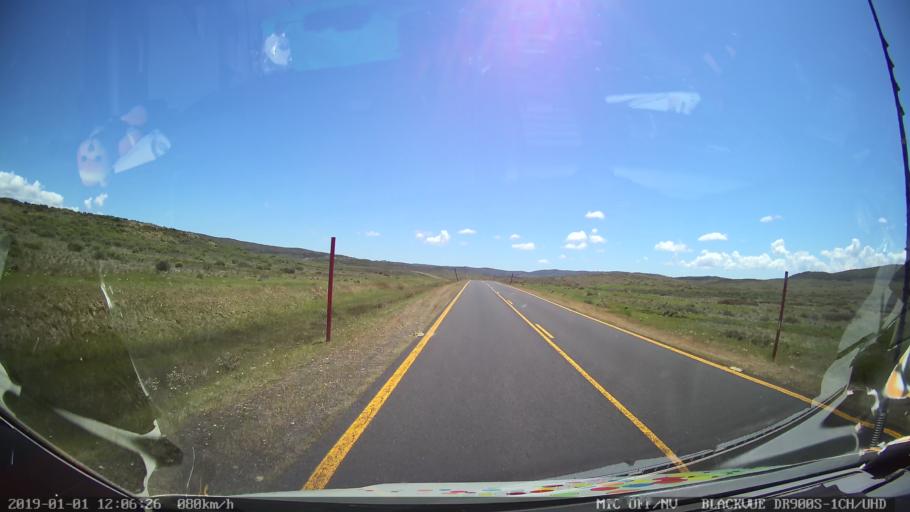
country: AU
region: New South Wales
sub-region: Snowy River
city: Jindabyne
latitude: -35.8450
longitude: 148.4913
